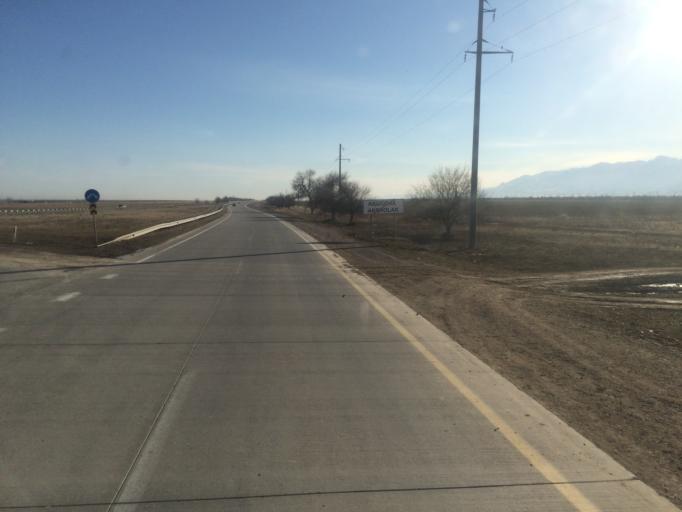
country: KZ
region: Zhambyl
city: Sarykemer
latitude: 43.0080
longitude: 71.8158
